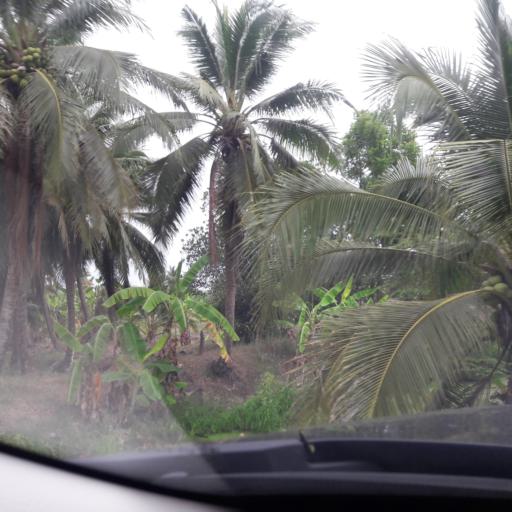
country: TH
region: Ratchaburi
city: Damnoen Saduak
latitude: 13.5808
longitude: 99.9473
